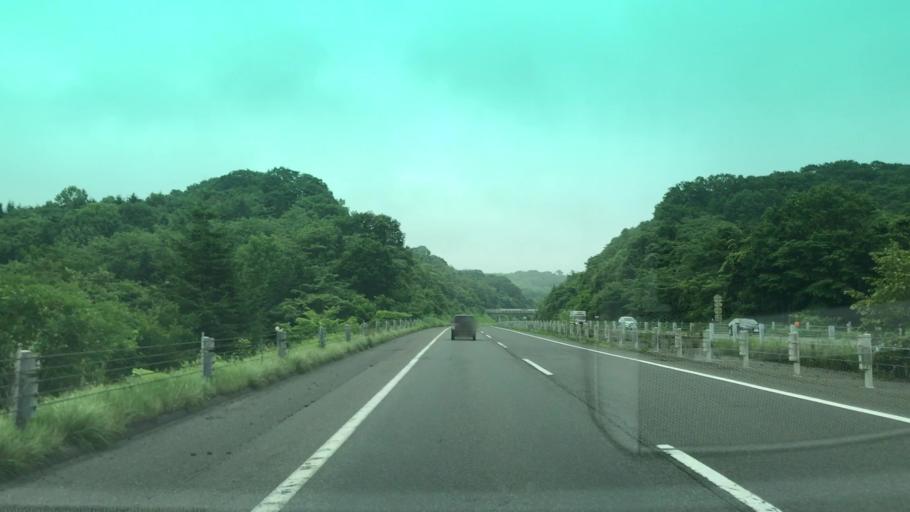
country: JP
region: Hokkaido
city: Shiraoi
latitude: 42.4782
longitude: 141.2192
